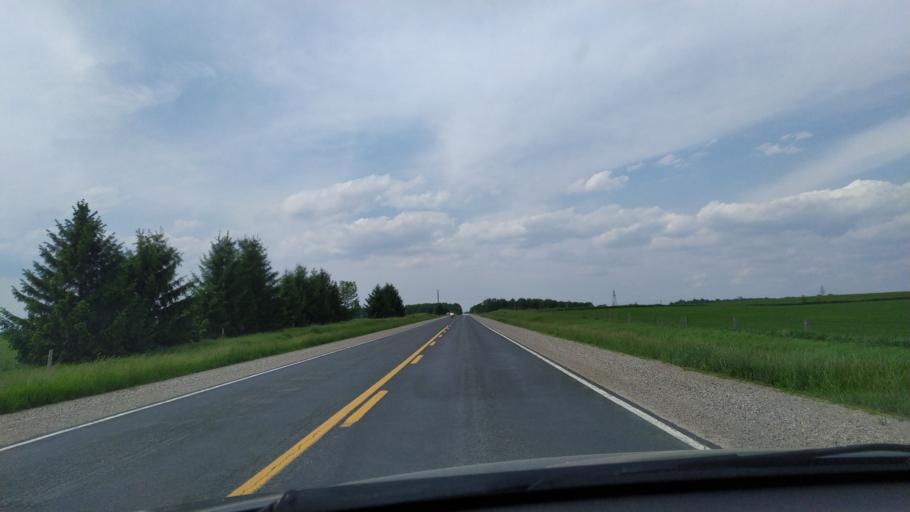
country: CA
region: Ontario
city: Ingersoll
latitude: 43.0334
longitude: -80.9746
